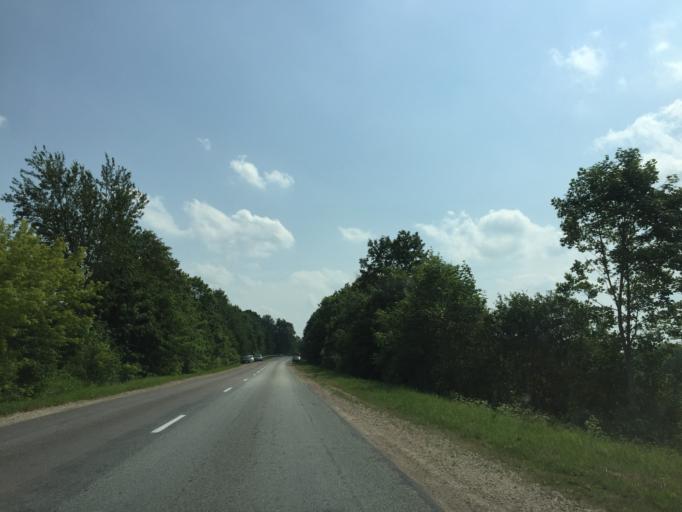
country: LV
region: Jelgava
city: Jelgava
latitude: 56.6909
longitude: 23.7191
